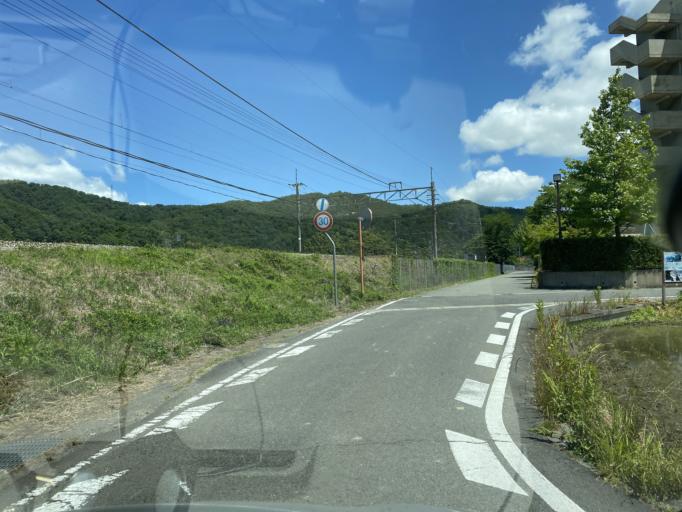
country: JP
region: Hyogo
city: Toyooka
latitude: 35.4948
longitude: 134.7994
